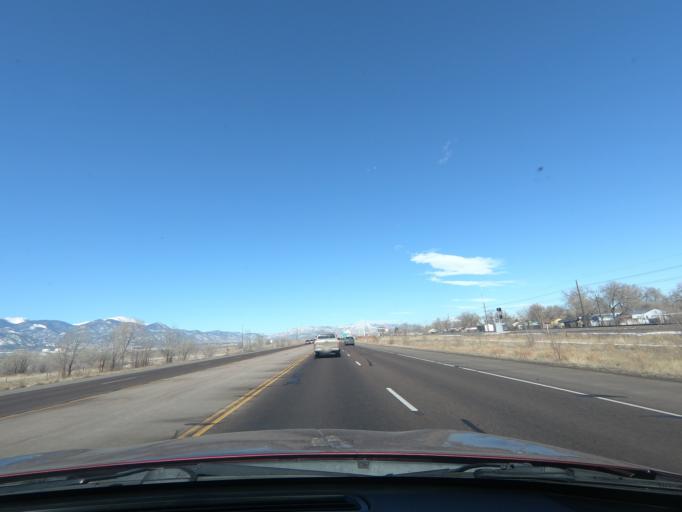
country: US
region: Colorado
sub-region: El Paso County
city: Stratmoor
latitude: 38.7621
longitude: -104.7543
